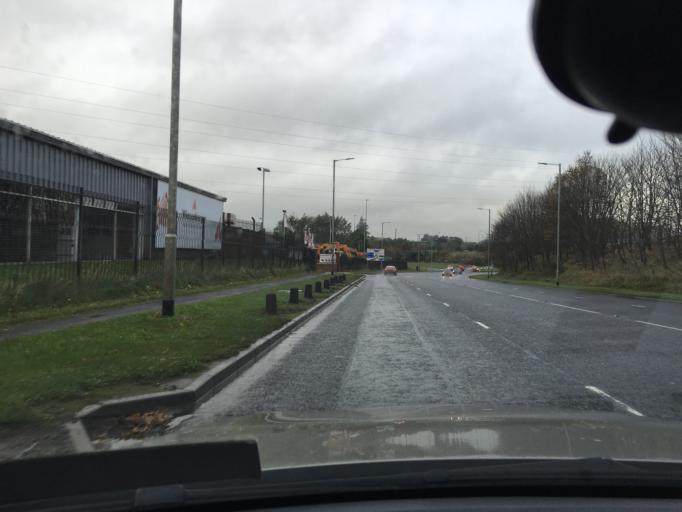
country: GB
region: Northern Ireland
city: Carnmoney
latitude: 54.6760
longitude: -5.9809
